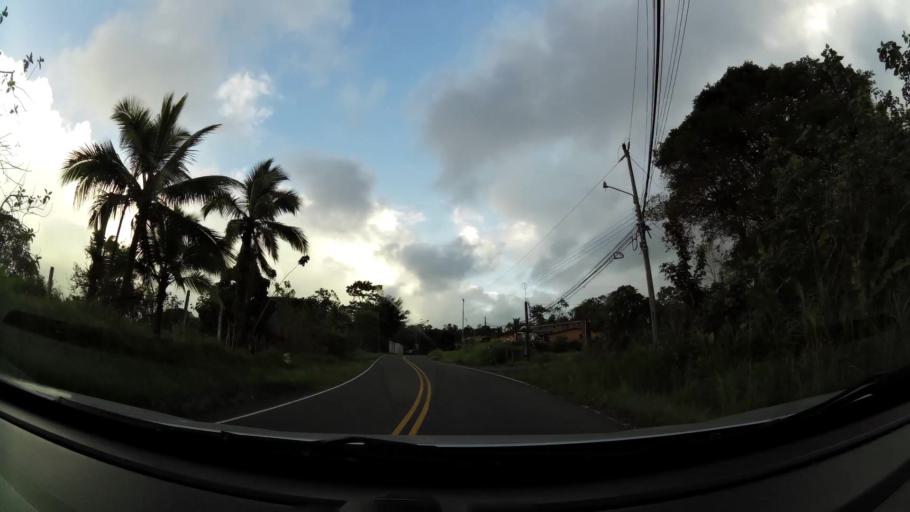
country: CR
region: Limon
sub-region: Canton de Siquirres
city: Siquirres
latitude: 9.9853
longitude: -83.5707
